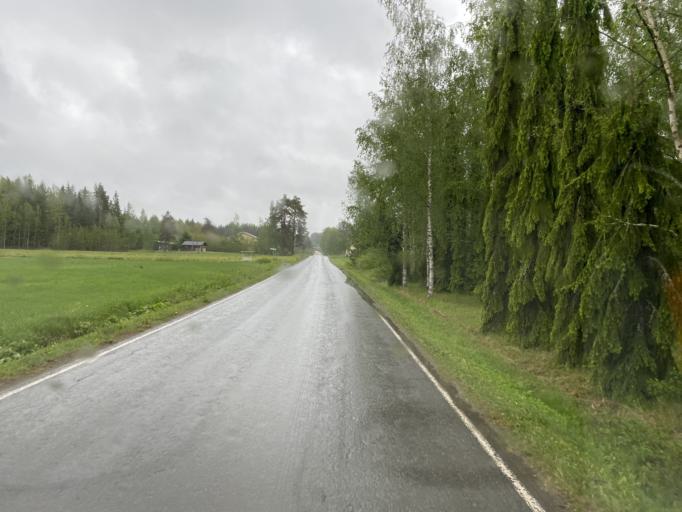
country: FI
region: Pirkanmaa
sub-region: Etelae-Pirkanmaa
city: Urjala
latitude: 60.9637
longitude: 23.5137
